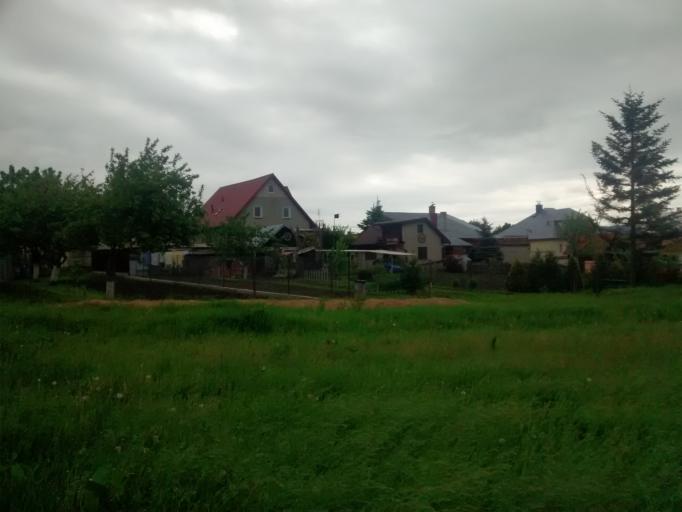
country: SK
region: Zilinsky
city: Ruzomberok
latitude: 49.0938
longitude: 19.3481
